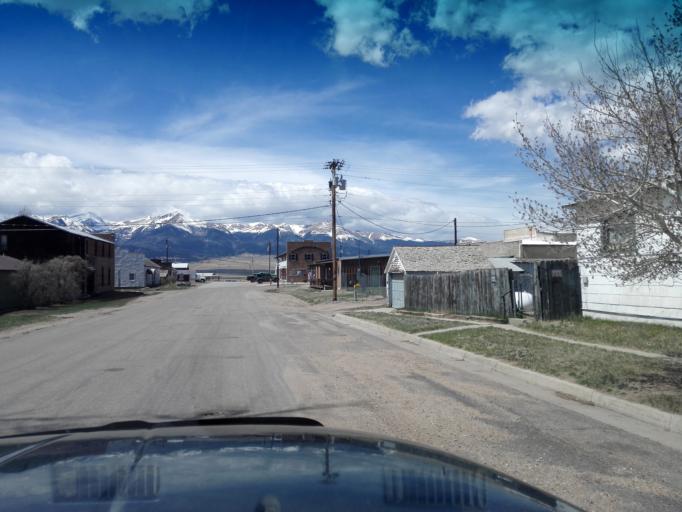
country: US
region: Colorado
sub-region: Custer County
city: Westcliffe
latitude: 38.1349
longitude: -105.4676
